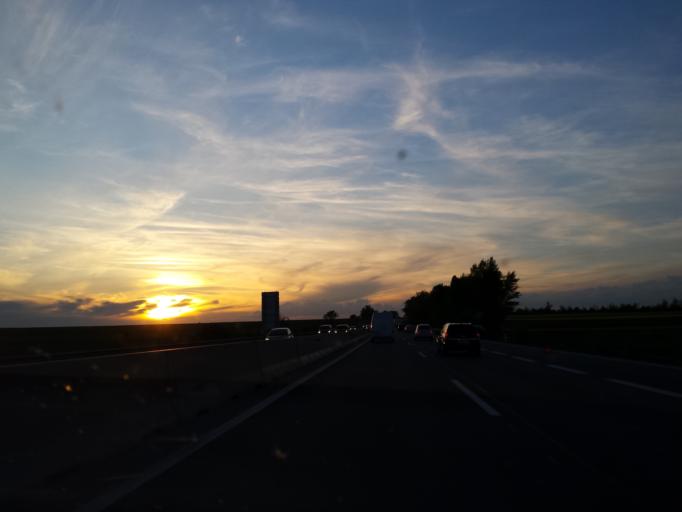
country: AT
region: Lower Austria
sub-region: Politischer Bezirk Wien-Umgebung
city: Fischamend Dorf
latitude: 48.0972
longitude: 16.6566
